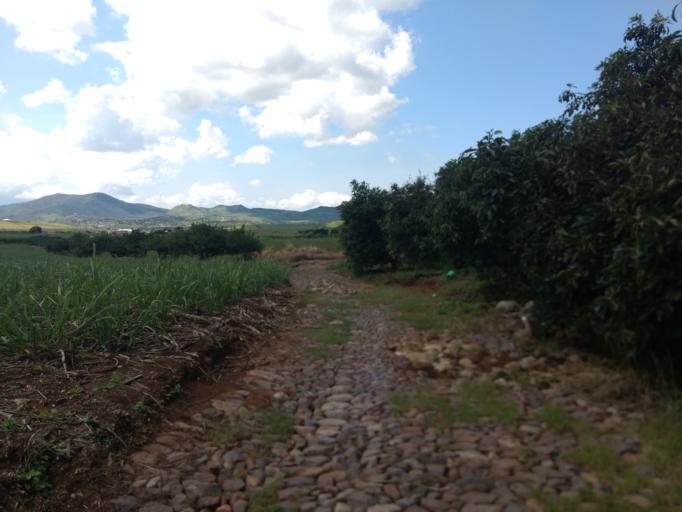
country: MX
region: Nayarit
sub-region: Tepic
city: La Corregidora
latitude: 21.4930
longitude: -104.7820
